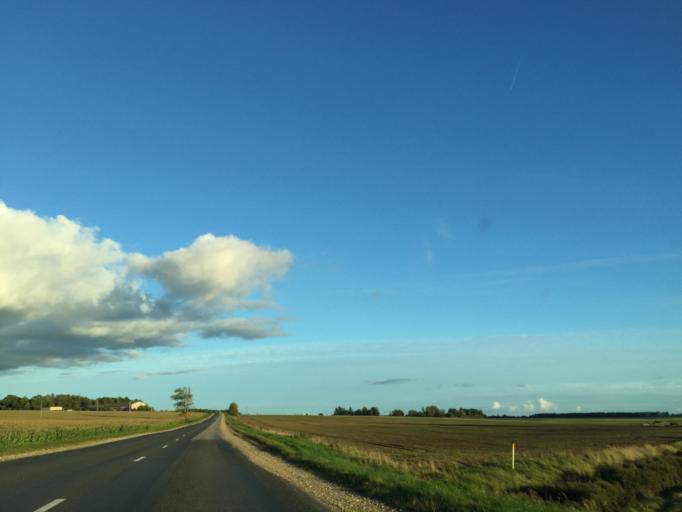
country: LV
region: Saldus Rajons
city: Saldus
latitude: 56.7106
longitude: 22.4149
